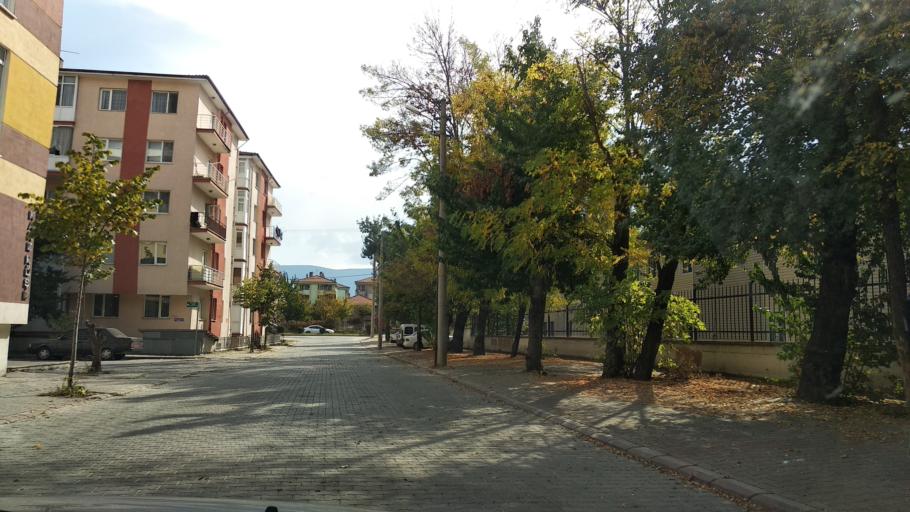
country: TR
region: Bolu
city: Bolu
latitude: 40.7393
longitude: 31.6043
